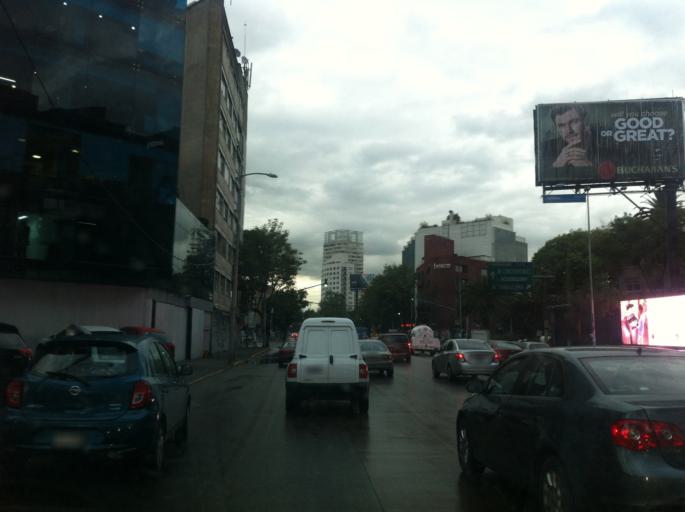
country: MX
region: Mexico City
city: Benito Juarez
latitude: 19.4061
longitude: -99.1782
